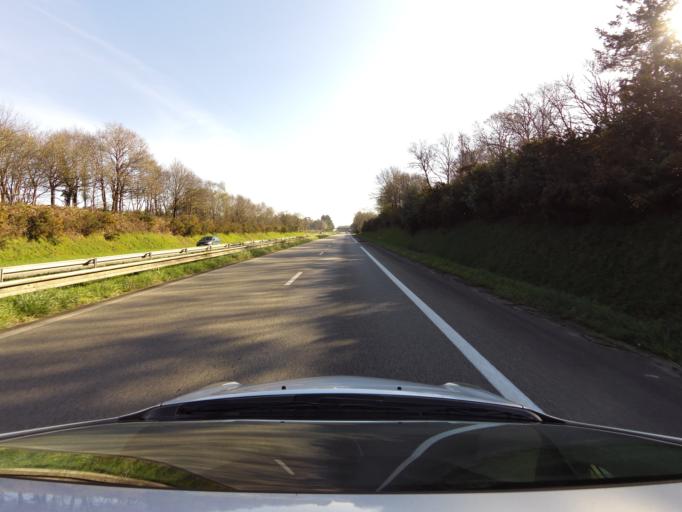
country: FR
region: Brittany
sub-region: Departement du Morbihan
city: Branderion
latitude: 47.8229
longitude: -3.2084
